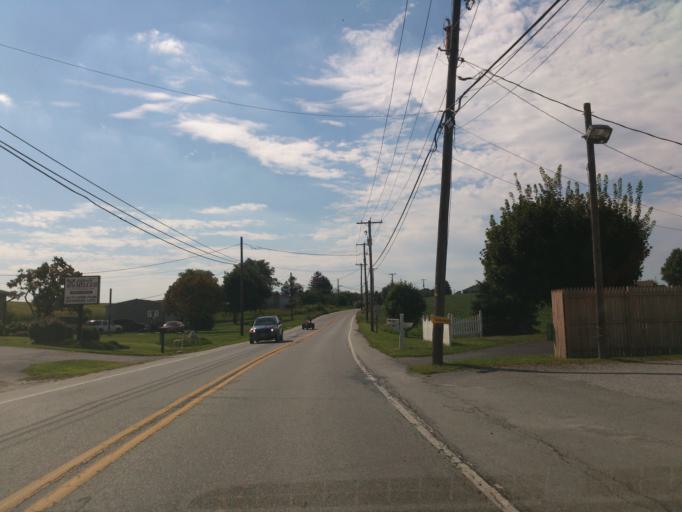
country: US
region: Pennsylvania
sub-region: York County
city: Windsor
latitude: 39.8817
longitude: -76.5365
